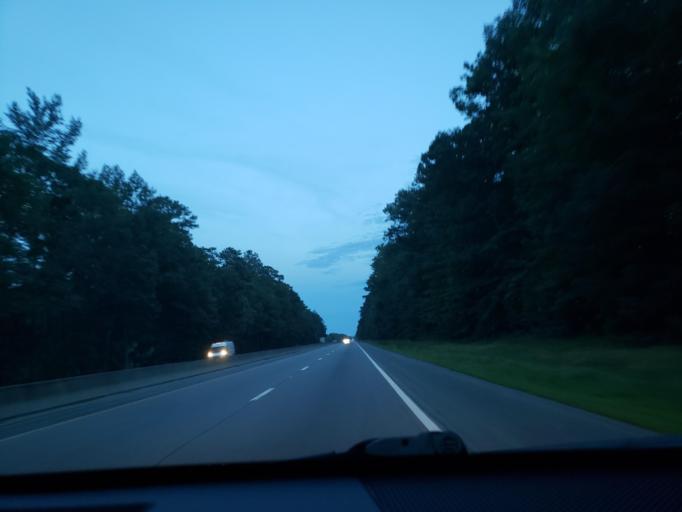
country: US
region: Virginia
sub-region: City of Franklin
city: Franklin
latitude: 36.6585
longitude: -76.9340
